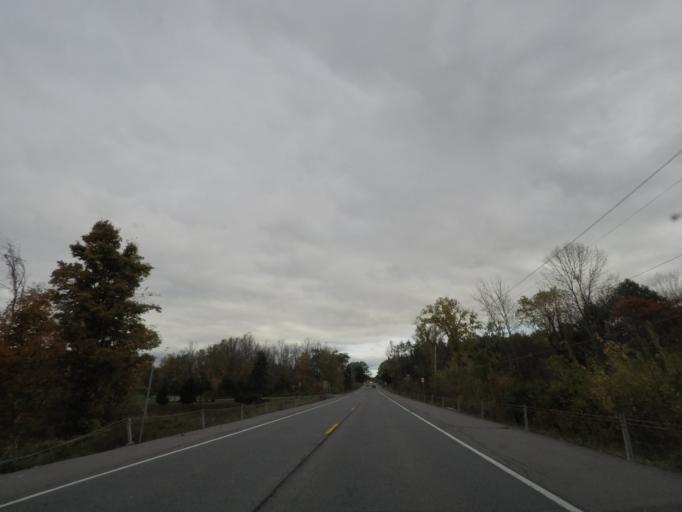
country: US
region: New York
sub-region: Saratoga County
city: Mechanicville
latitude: 42.8640
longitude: -73.7264
